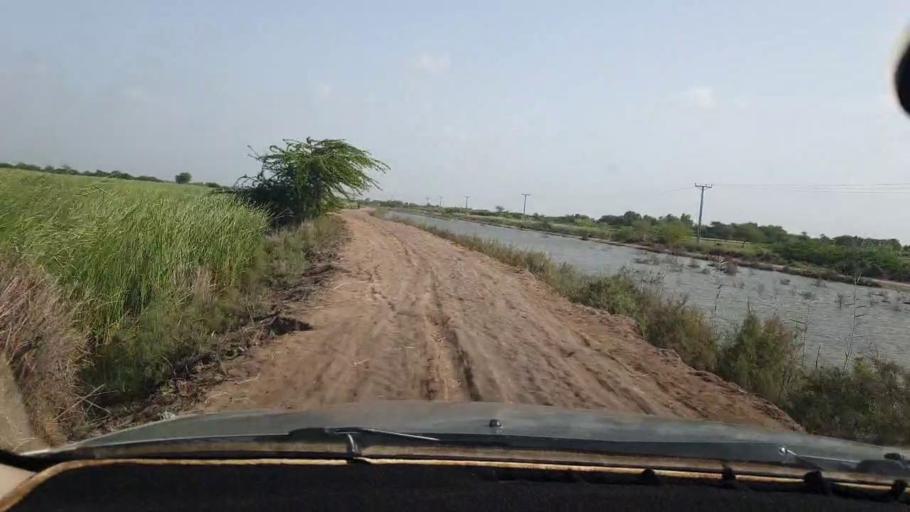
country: PK
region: Sindh
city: Tando Bago
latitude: 24.8131
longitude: 68.9356
